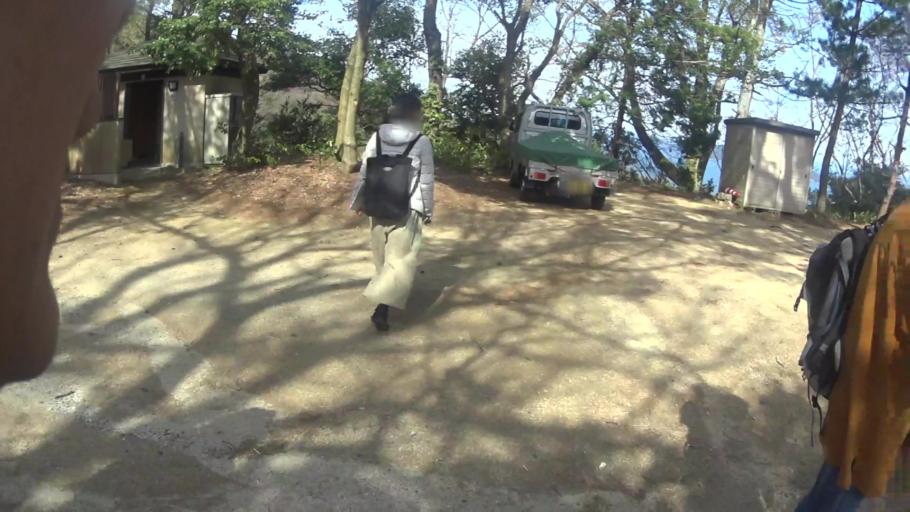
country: JP
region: Kyoto
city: Miyazu
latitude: 35.5871
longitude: 135.1942
